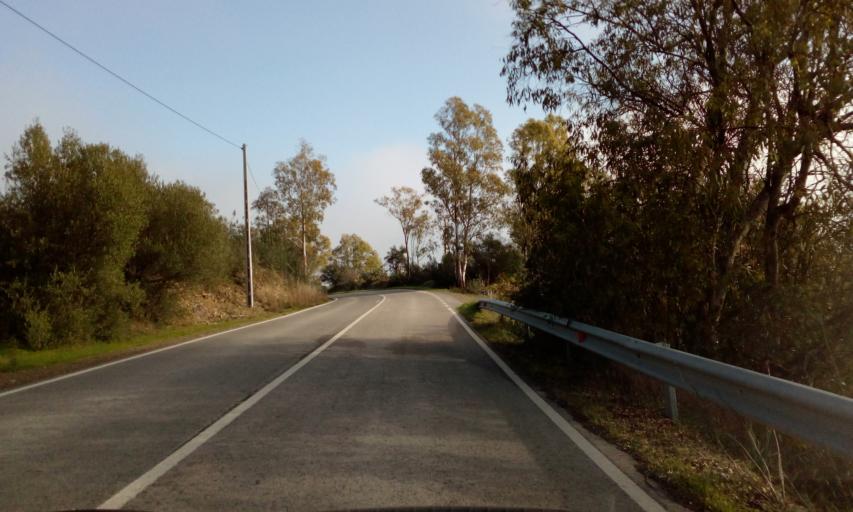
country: PT
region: Faro
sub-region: Alcoutim
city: Alcoutim
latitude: 37.4470
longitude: -7.4917
